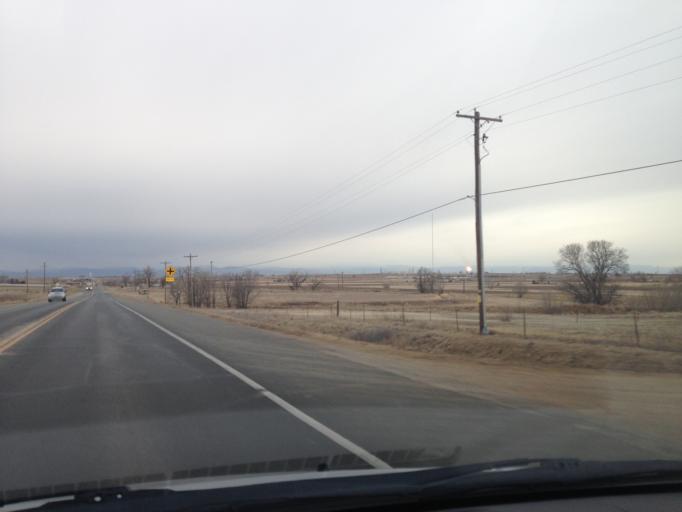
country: US
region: Colorado
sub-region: Weld County
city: Fort Lupton
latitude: 40.0800
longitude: -104.8638
